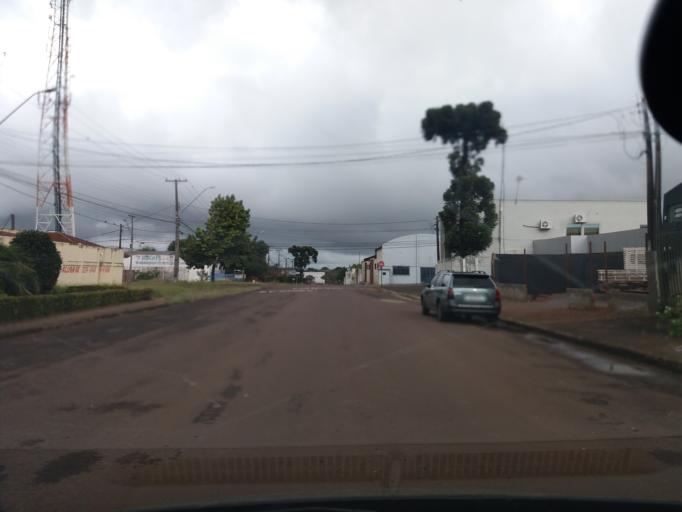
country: BR
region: Parana
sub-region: Cascavel
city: Cascavel
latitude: -24.9774
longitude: -53.4527
